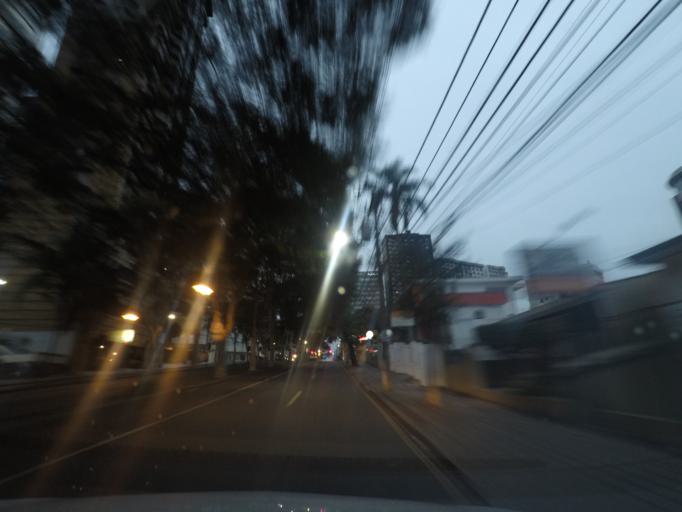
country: BR
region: Parana
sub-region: Curitiba
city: Curitiba
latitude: -25.4298
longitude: -49.2917
